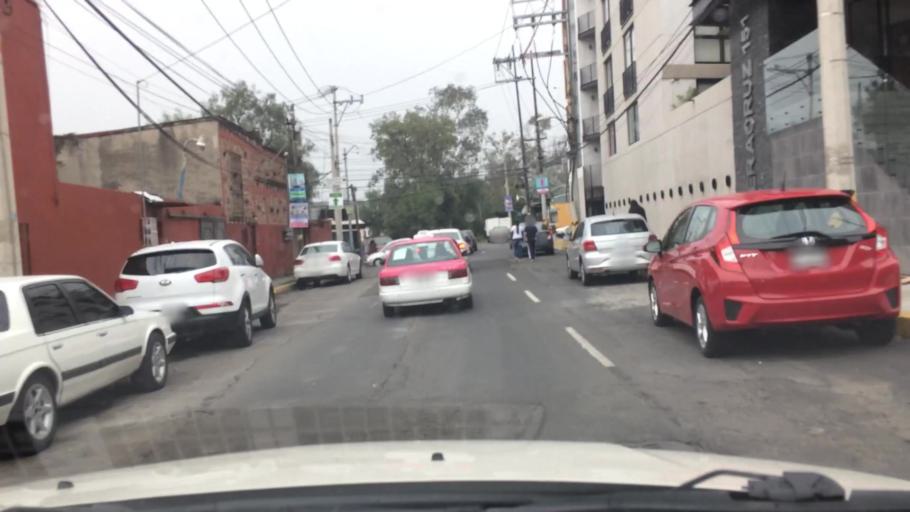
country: MX
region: Mexico City
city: Magdalena Contreras
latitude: 19.3420
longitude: -99.2048
